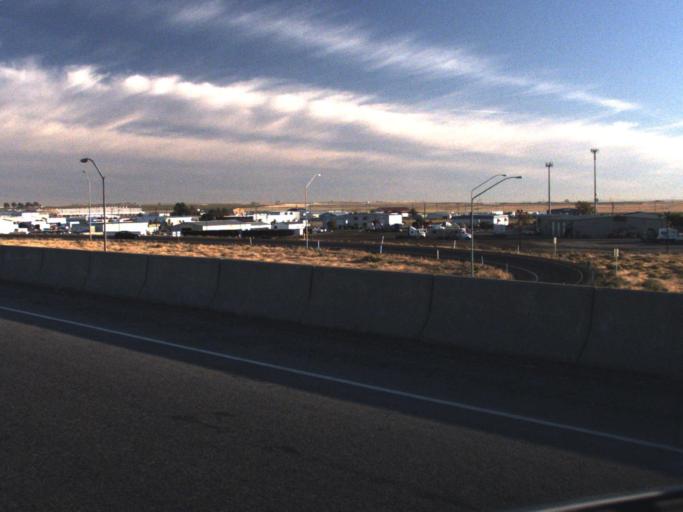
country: US
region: Washington
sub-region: Franklin County
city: Pasco
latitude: 46.2516
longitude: -119.0826
